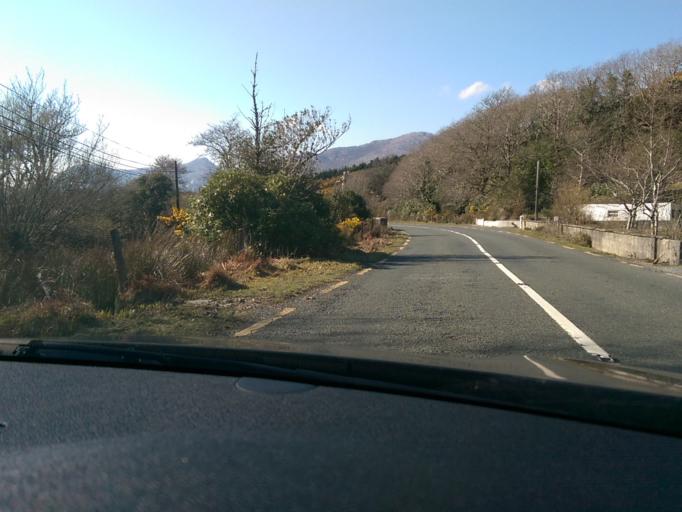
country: IE
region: Connaught
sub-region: County Galway
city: Clifden
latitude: 53.4662
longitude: -9.7265
